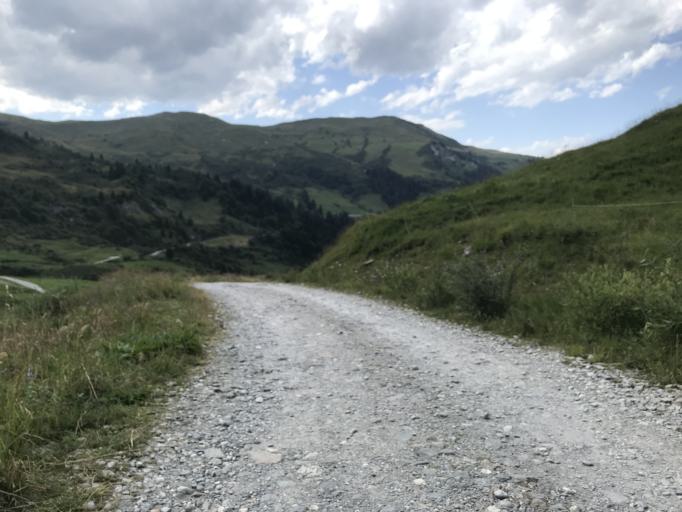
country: FR
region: Rhone-Alpes
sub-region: Departement de la Savoie
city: Beaufort
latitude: 45.6614
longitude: 6.6304
